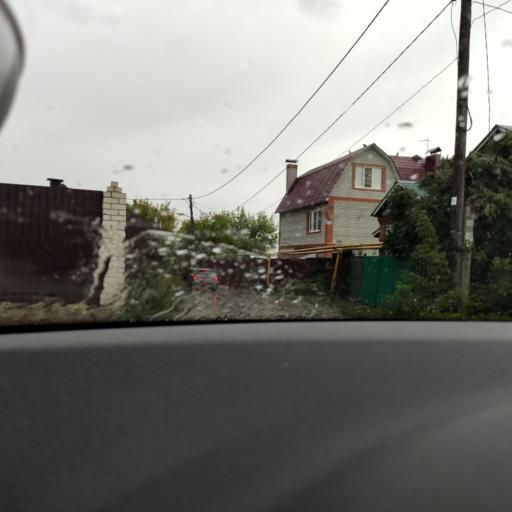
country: RU
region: Samara
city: Samara
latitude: 53.1753
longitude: 50.1524
